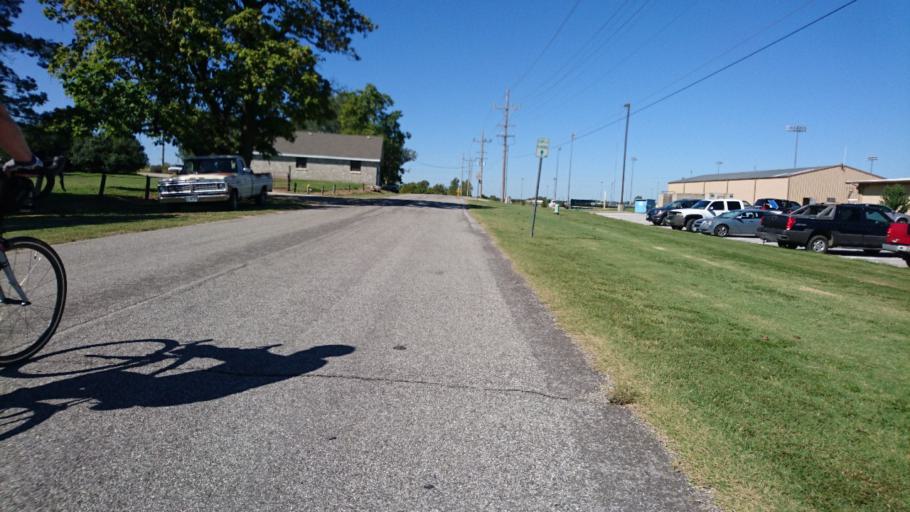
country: US
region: Missouri
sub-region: Jasper County
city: Joplin
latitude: 37.0920
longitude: -94.5550
